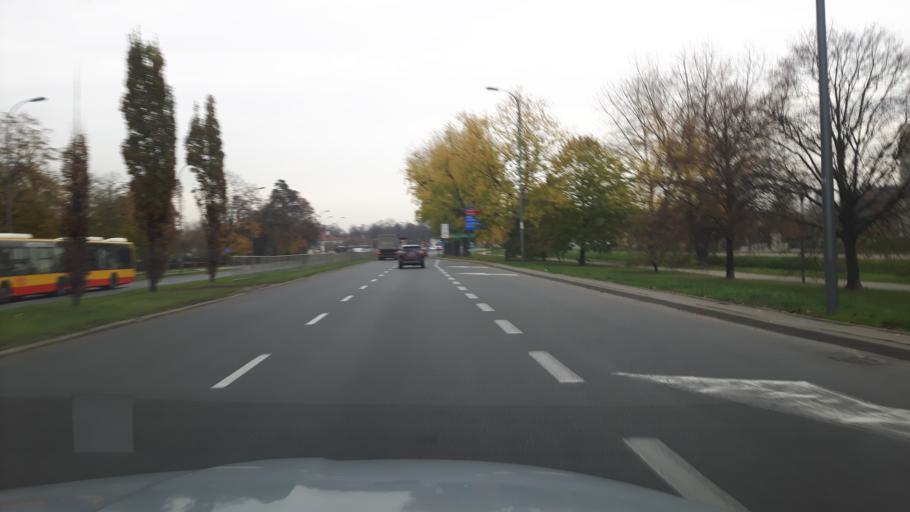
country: PL
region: Masovian Voivodeship
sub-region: Warszawa
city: Wilanow
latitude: 52.1669
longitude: 21.0801
